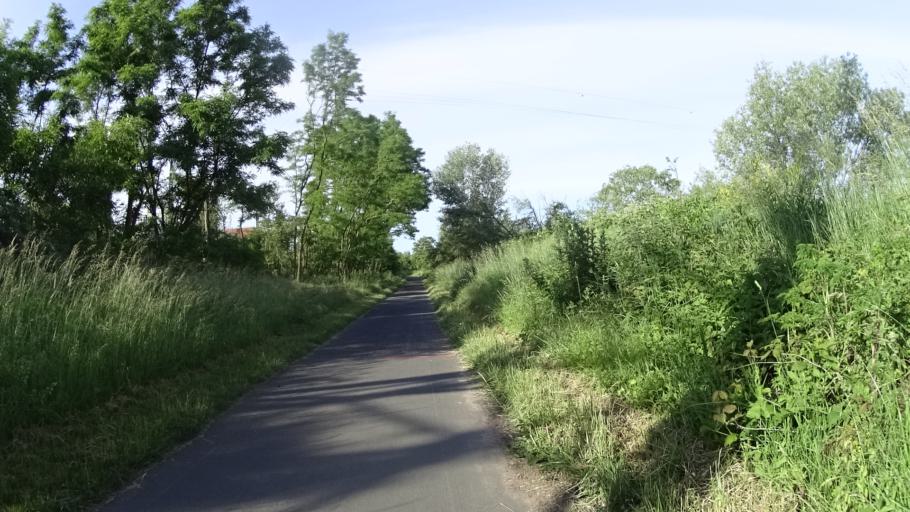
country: DE
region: Hesse
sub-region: Regierungsbezirk Darmstadt
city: Seligenstadt
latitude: 50.0581
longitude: 8.9852
